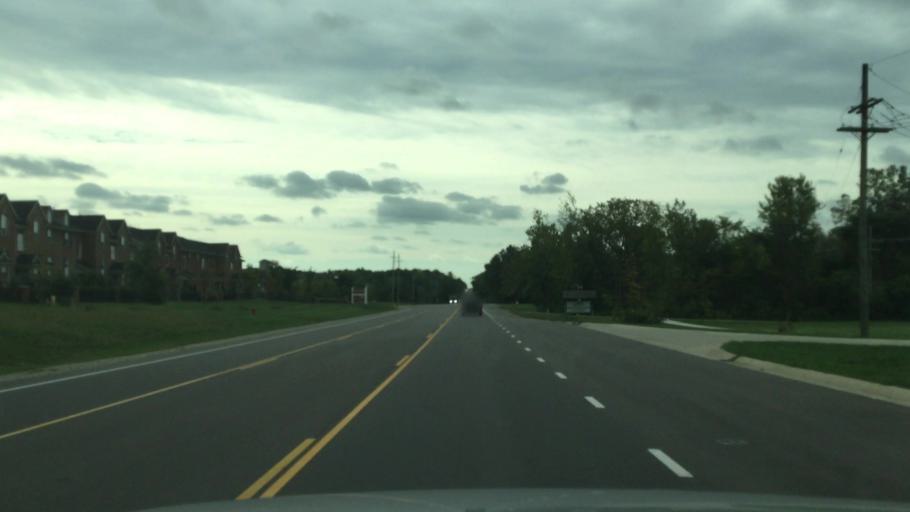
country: US
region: Michigan
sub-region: Livingston County
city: Howell
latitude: 42.6257
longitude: -83.8753
